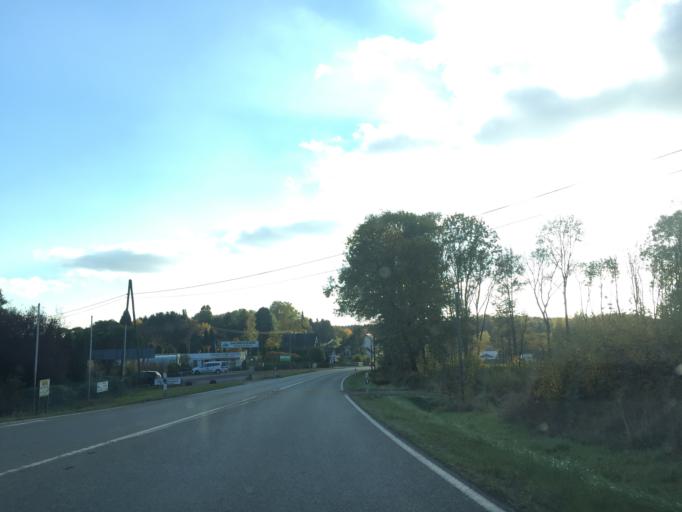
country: DE
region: Rheinland-Pfalz
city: Weroth
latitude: 50.4504
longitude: 7.9443
